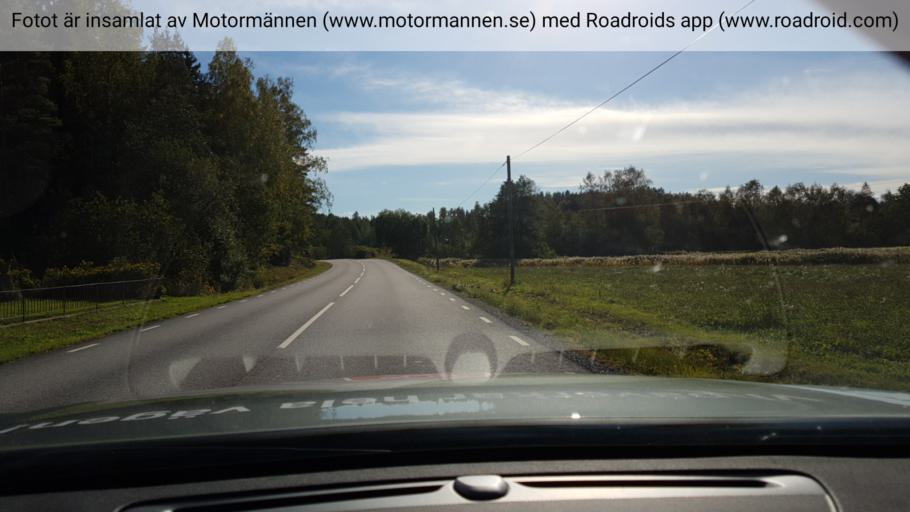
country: SE
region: OEstergoetland
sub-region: Valdemarsviks Kommun
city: Valdemarsvik
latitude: 58.1836
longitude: 16.5803
